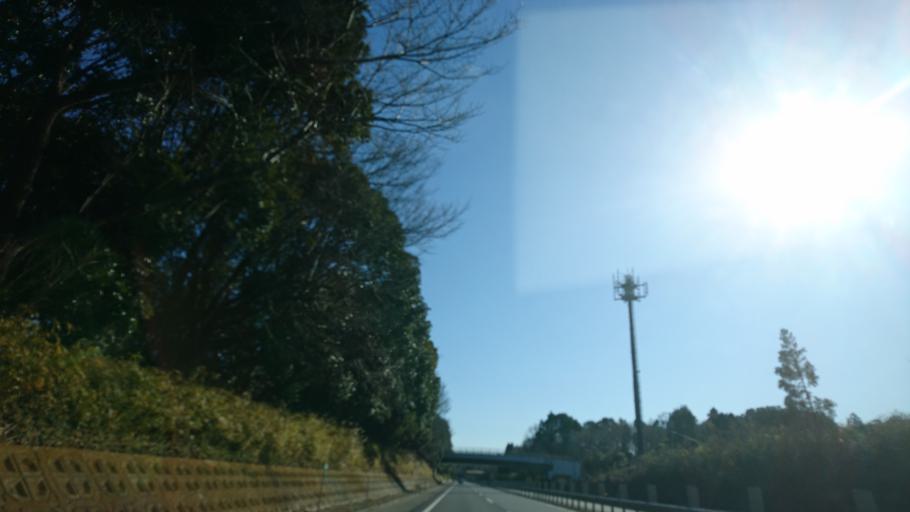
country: JP
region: Chiba
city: Chiba
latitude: 35.5787
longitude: 140.1914
